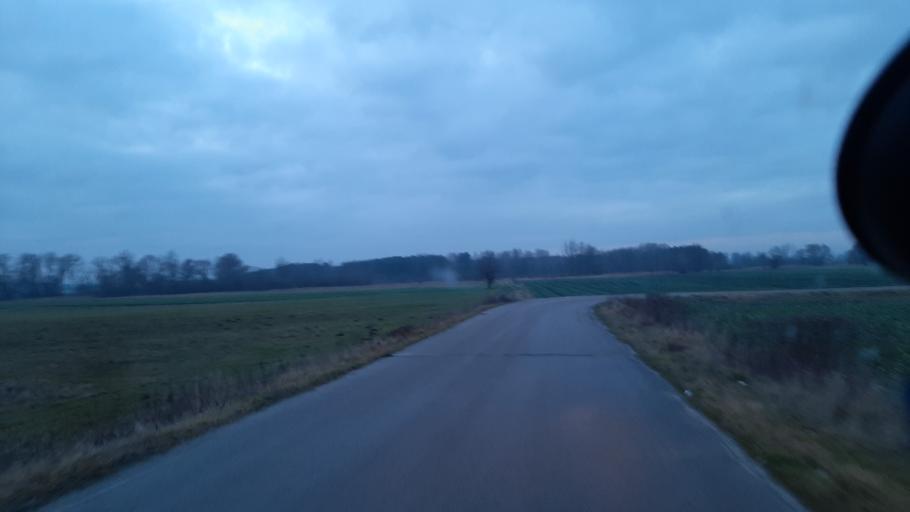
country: PL
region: Lublin Voivodeship
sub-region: Powiat lubartowski
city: Firlej
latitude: 51.5773
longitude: 22.5395
